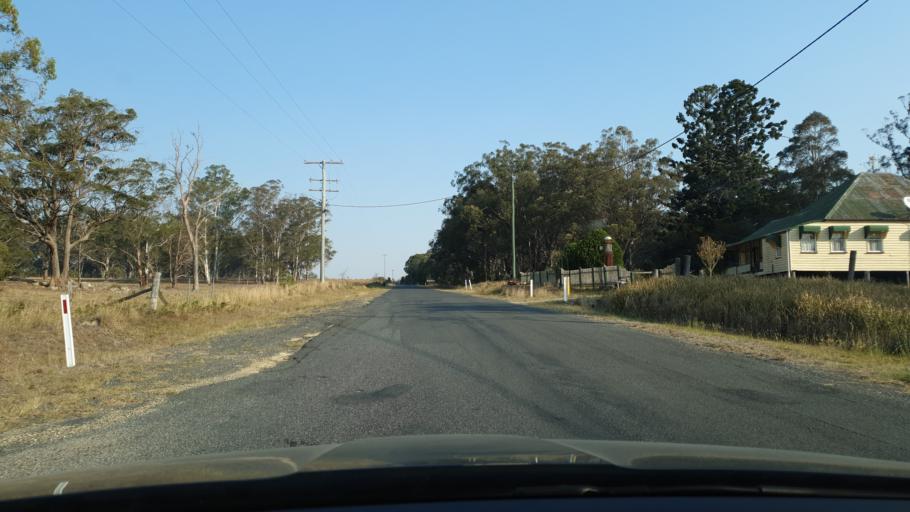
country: AU
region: New South Wales
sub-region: Tenterfield Municipality
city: Carrolls Creek
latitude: -28.6899
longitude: 152.0869
